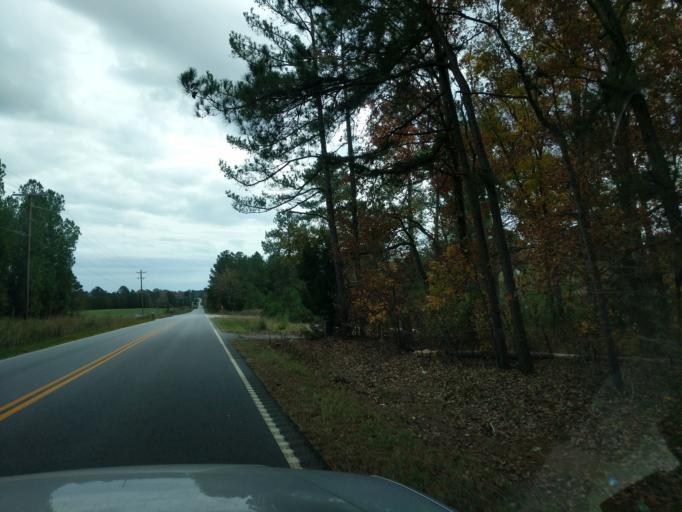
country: US
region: South Carolina
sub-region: Saluda County
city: Saluda
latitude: 34.0285
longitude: -81.7999
